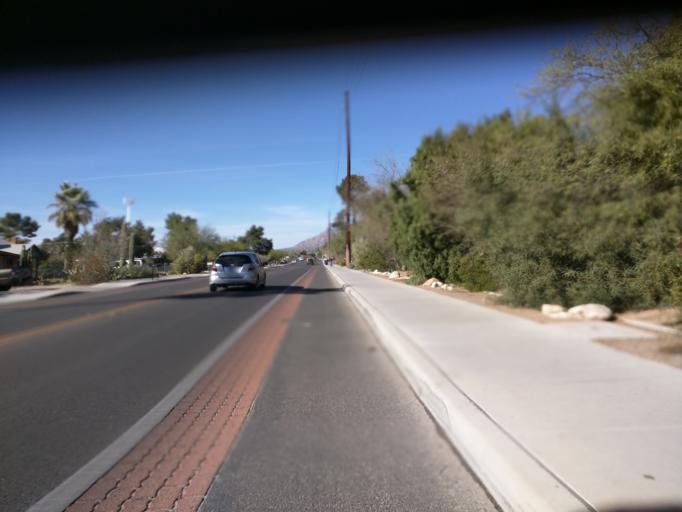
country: US
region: Arizona
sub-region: Pima County
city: Catalina Foothills
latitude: 32.2688
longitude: -110.9523
